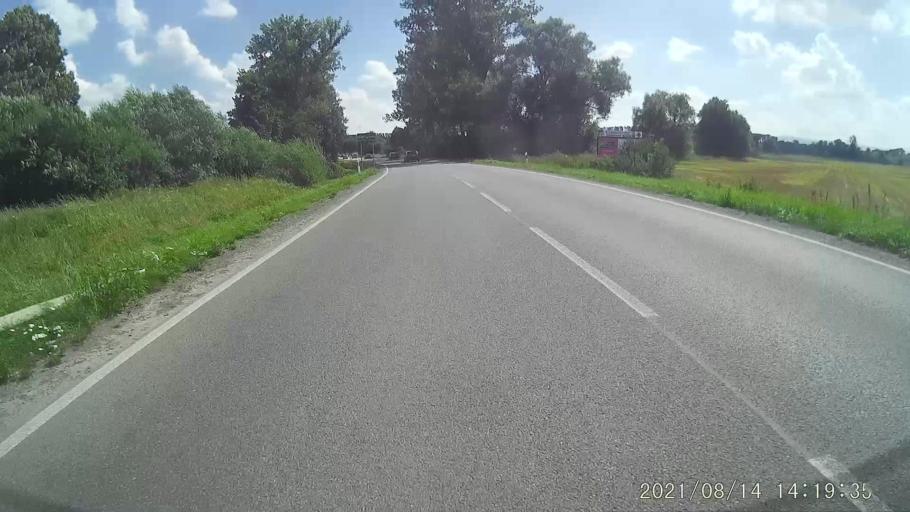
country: PL
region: Lower Silesian Voivodeship
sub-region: Powiat klodzki
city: Klodzko
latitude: 50.4648
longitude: 16.6228
